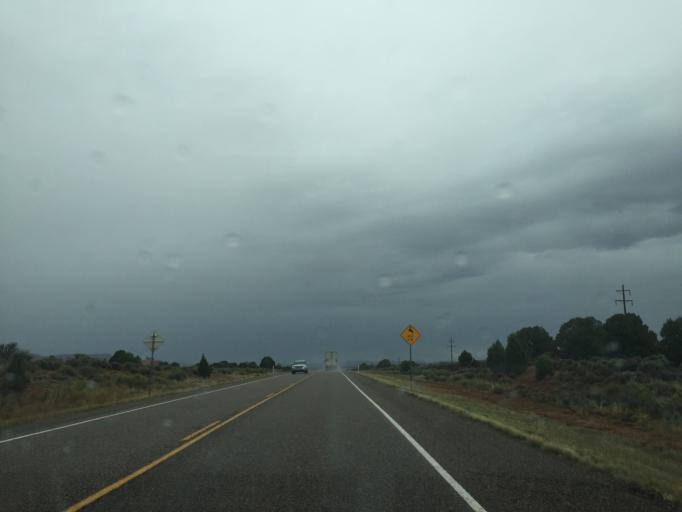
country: US
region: Utah
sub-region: Kane County
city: Kanab
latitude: 37.1043
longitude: -112.1269
